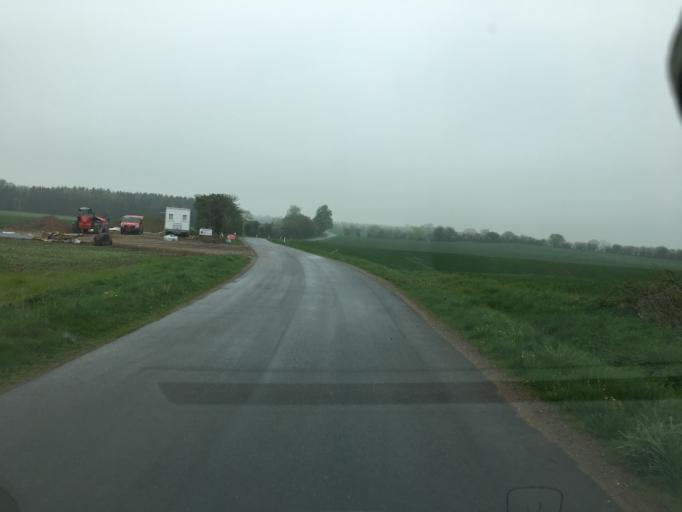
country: DK
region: South Denmark
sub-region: Haderslev Kommune
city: Haderslev
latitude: 55.2759
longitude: 9.4402
